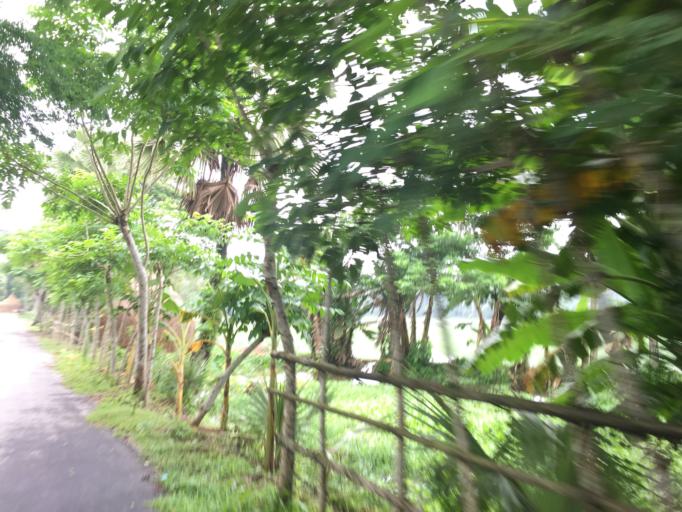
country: BD
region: Barisal
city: Mathba
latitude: 22.2102
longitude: 89.9298
